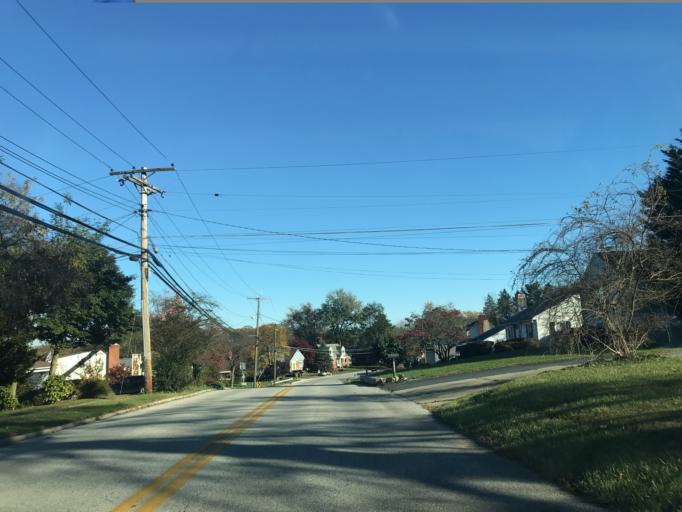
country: US
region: Maryland
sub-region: Baltimore County
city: Carney
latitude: 39.4146
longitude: -76.5183
